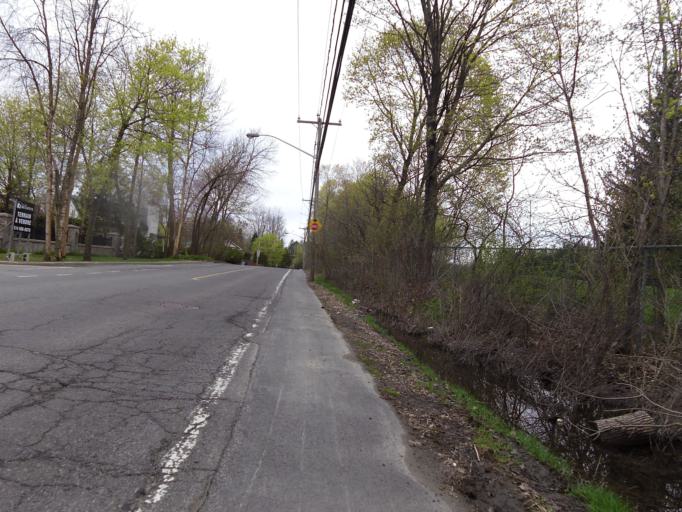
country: CA
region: Quebec
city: Dollard-Des Ormeaux
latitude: 45.5225
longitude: -73.8431
